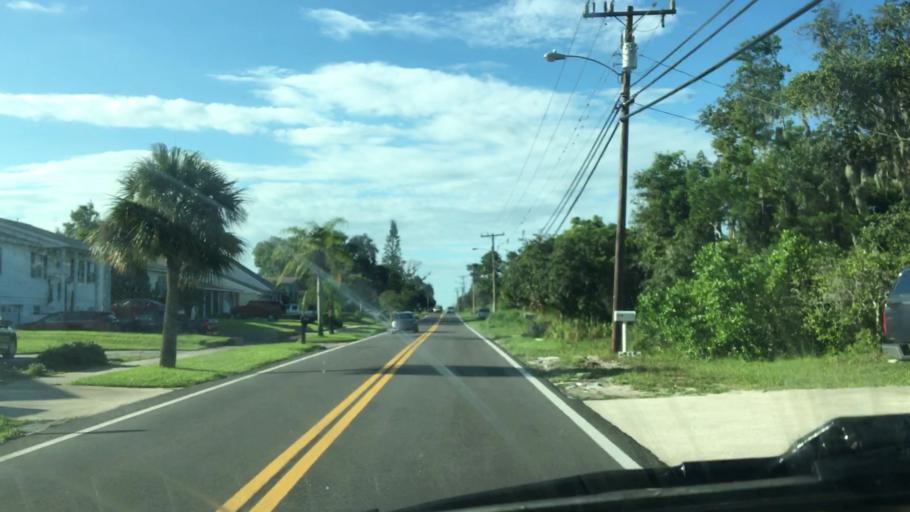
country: US
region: Florida
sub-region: Brevard County
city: Mims
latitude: 28.6211
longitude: -80.8603
